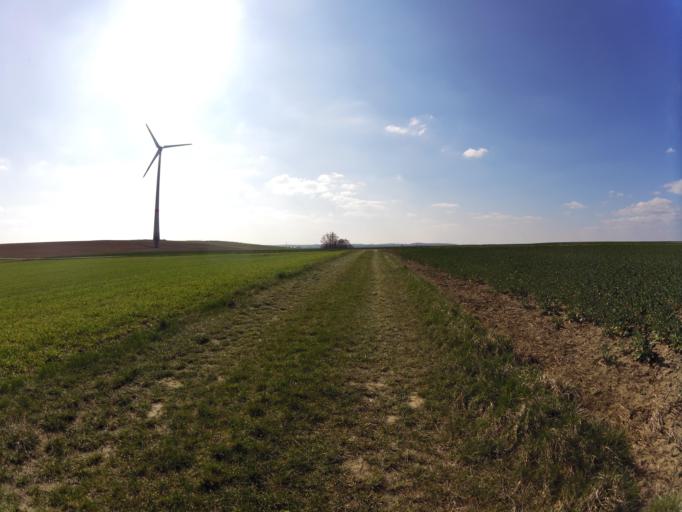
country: DE
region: Bavaria
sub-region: Regierungsbezirk Unterfranken
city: Nordheim
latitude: 49.8347
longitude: 10.1667
